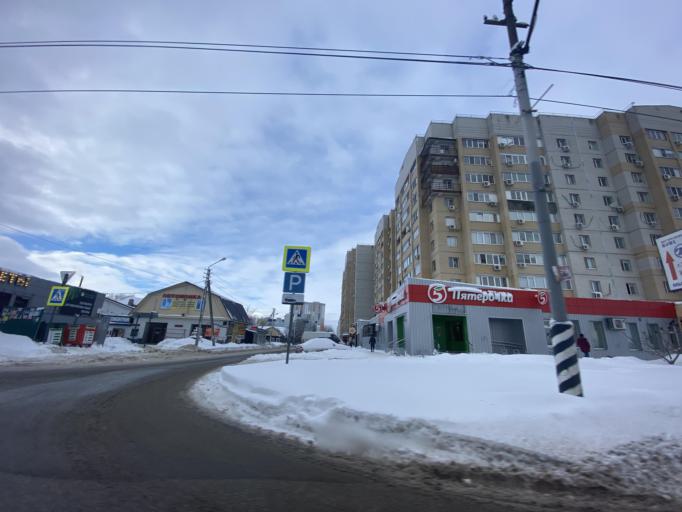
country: RU
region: Saratov
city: Engel's
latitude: 51.4977
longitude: 46.0952
